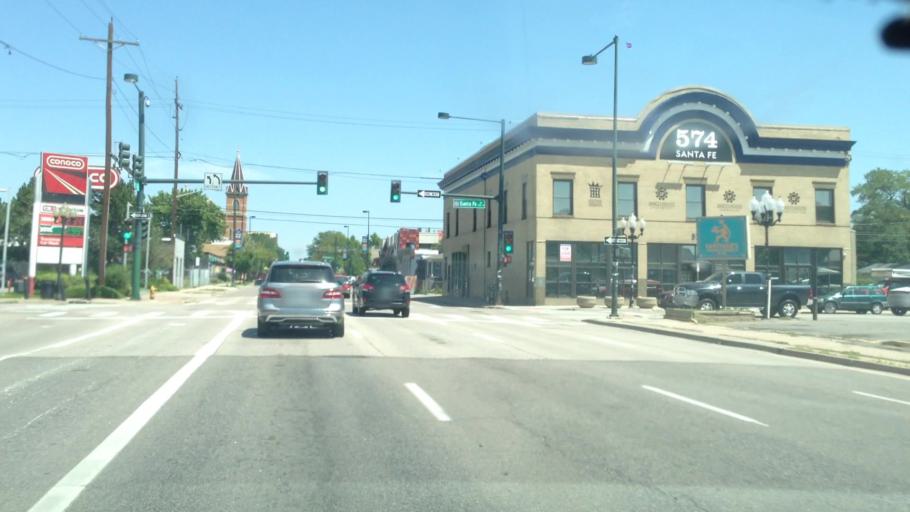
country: US
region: Colorado
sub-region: Denver County
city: Denver
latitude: 39.7257
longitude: -104.9990
